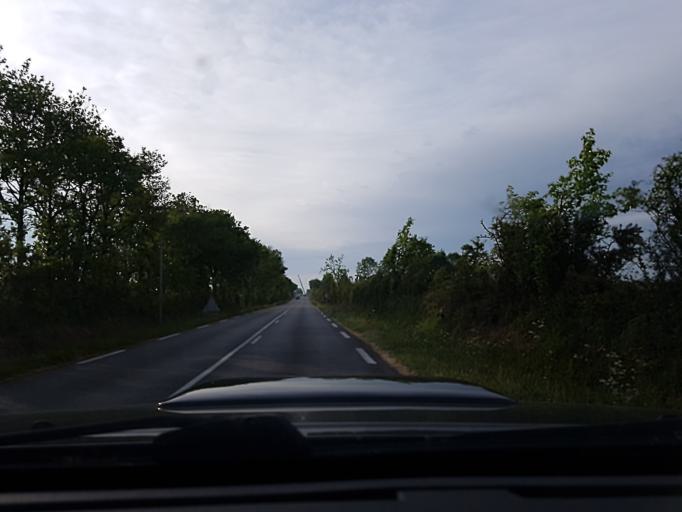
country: FR
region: Pays de la Loire
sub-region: Departement de la Vendee
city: Mache
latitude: 46.7673
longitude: -1.6609
